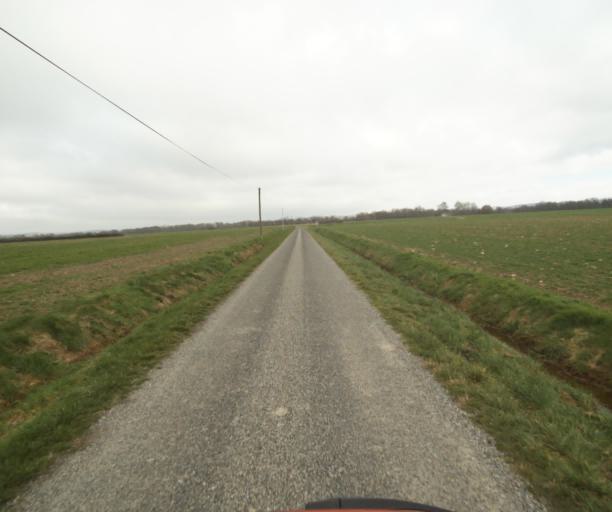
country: FR
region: Languedoc-Roussillon
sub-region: Departement de l'Aude
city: Belpech
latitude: 43.1805
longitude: 1.6919
